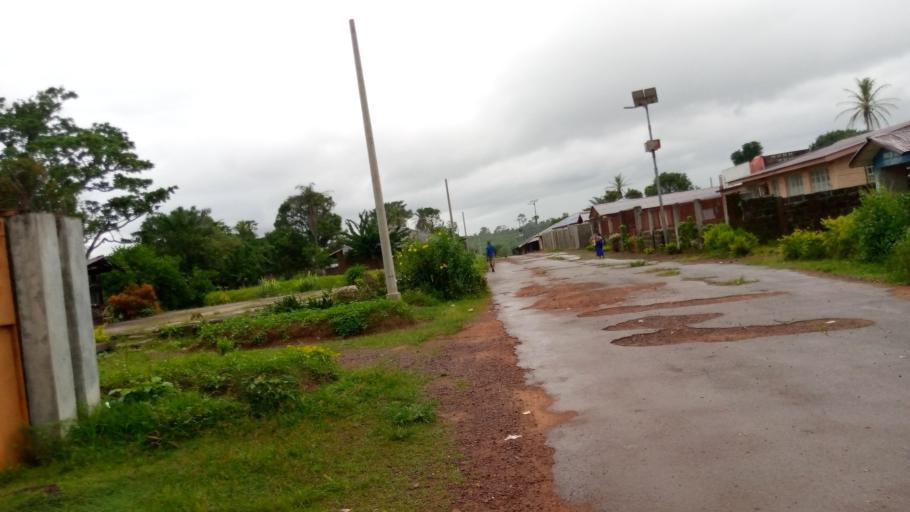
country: SL
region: Southern Province
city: Moyamba
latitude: 8.1624
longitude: -12.4370
